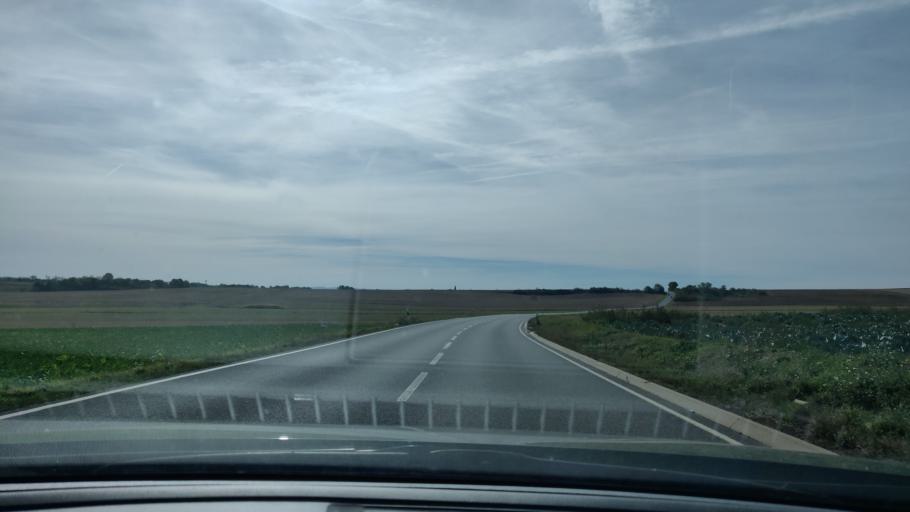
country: DE
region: Hesse
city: Fritzlar
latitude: 51.1559
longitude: 9.2741
